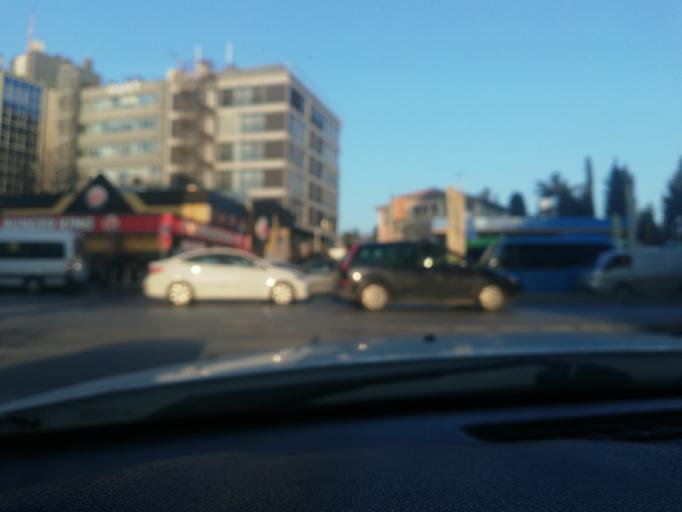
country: TR
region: Istanbul
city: Sisli
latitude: 41.0657
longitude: 28.9869
